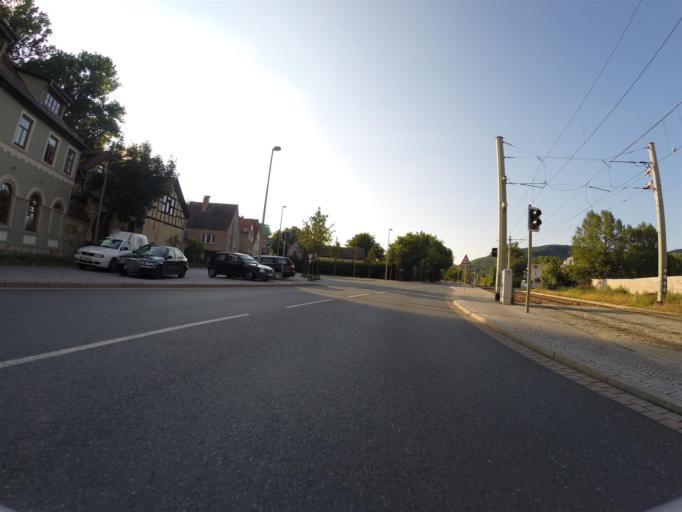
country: DE
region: Thuringia
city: Jena
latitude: 50.8957
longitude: 11.5969
